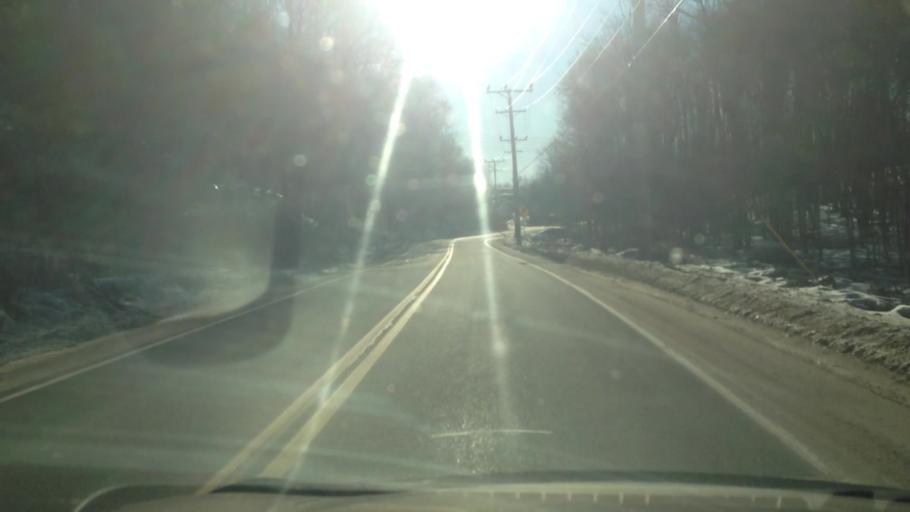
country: CA
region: Quebec
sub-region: Laurentides
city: Mont-Tremblant
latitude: 46.0223
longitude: -74.6084
